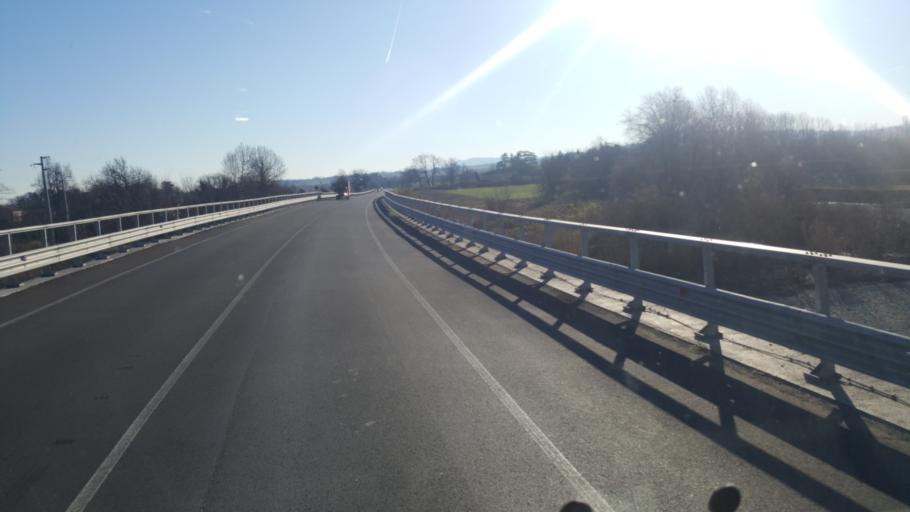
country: IT
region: Emilia-Romagna
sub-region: Provincia di Bologna
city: Bazzano
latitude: 44.5144
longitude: 11.0795
